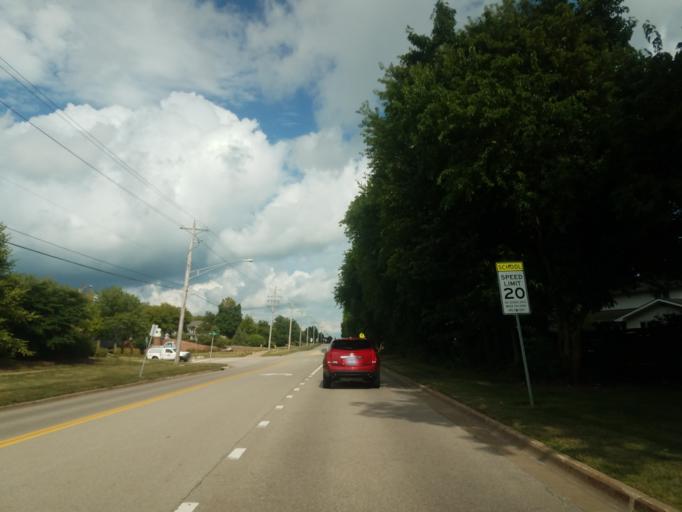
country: US
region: Illinois
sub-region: McLean County
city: Normal
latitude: 40.5104
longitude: -88.9387
